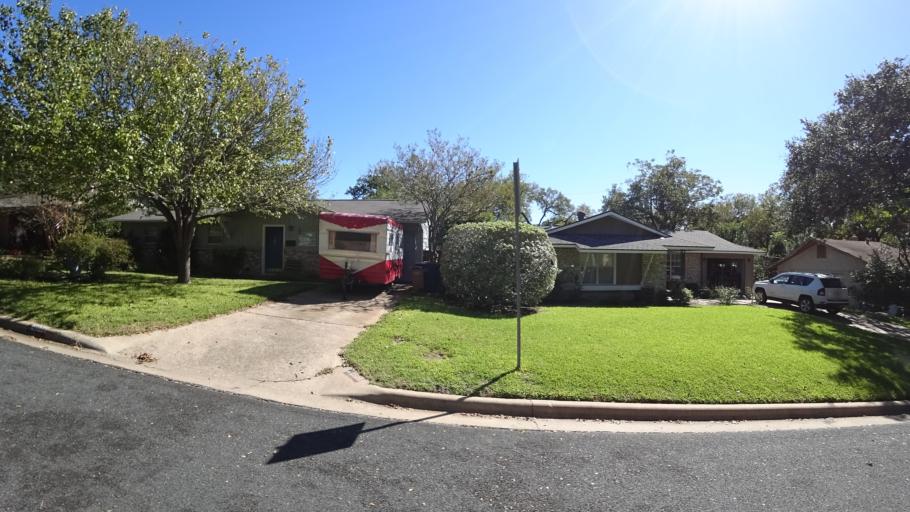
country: US
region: Texas
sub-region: Travis County
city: Rollingwood
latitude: 30.2208
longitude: -97.7906
